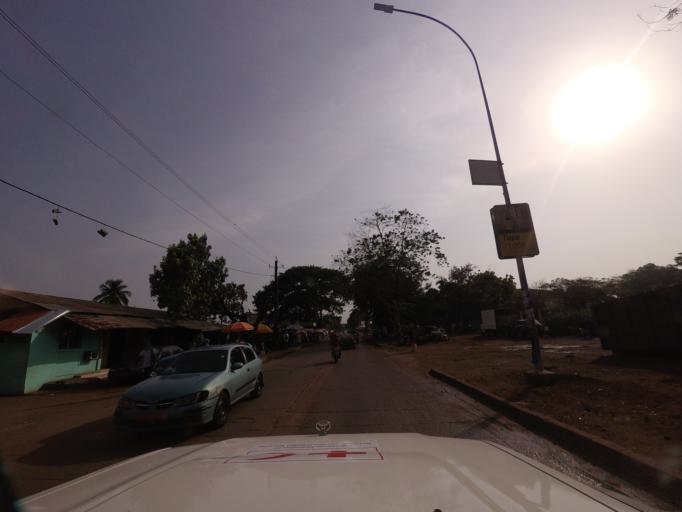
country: GN
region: Conakry
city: Camayenne
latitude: 9.5348
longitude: -13.6855
